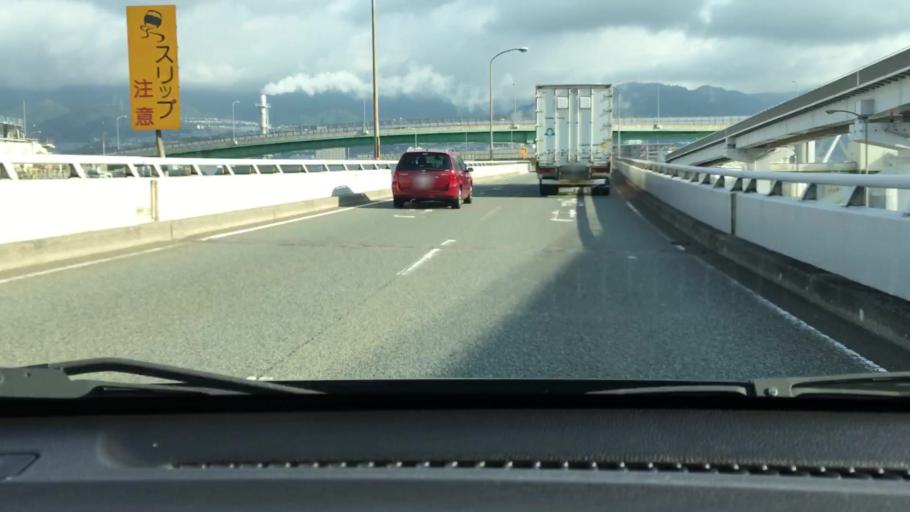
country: JP
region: Hyogo
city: Ashiya
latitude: 34.7036
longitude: 135.2670
